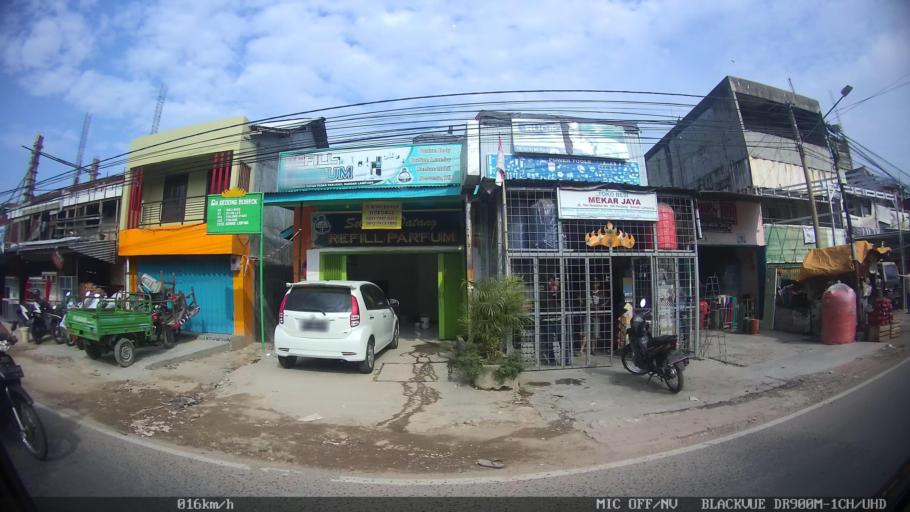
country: ID
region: Lampung
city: Panjang
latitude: -5.4723
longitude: 105.3221
